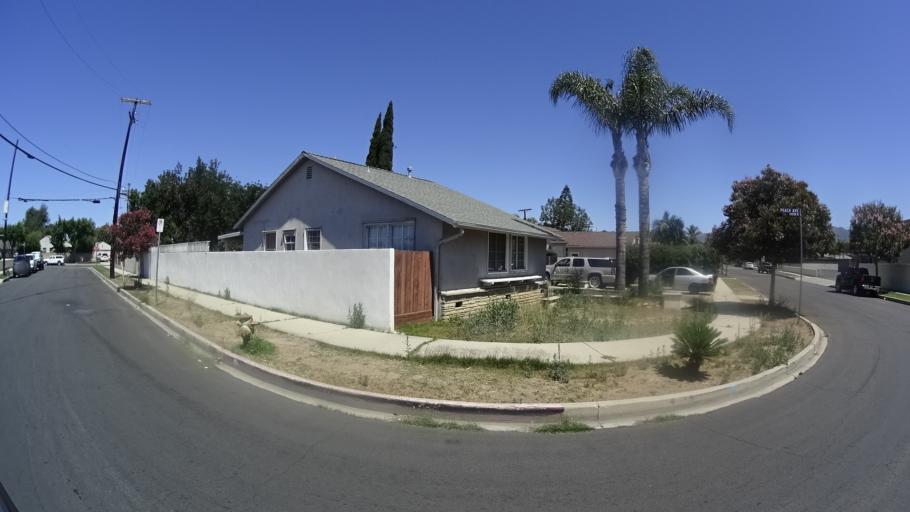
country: US
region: California
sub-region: Los Angeles County
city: San Fernando
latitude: 34.2587
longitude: -118.4687
